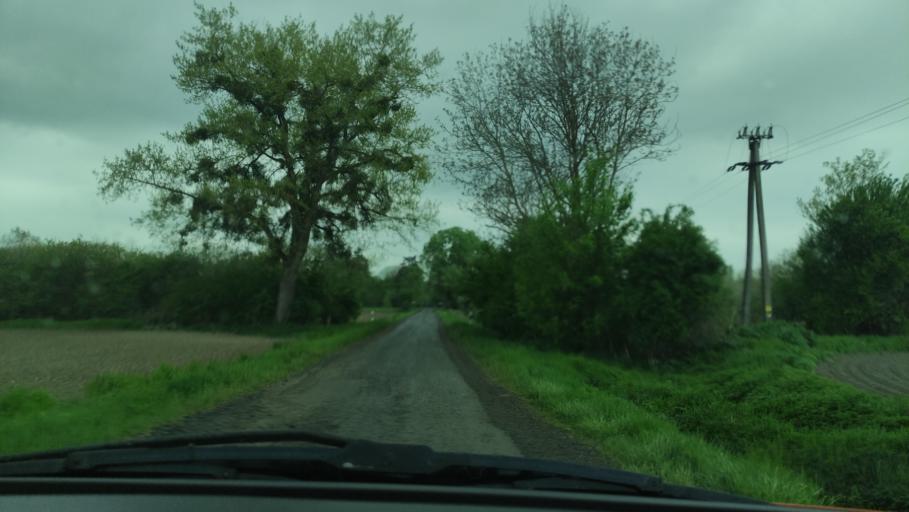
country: HR
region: Osjecko-Baranjska
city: Batina
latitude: 45.9057
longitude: 18.7652
